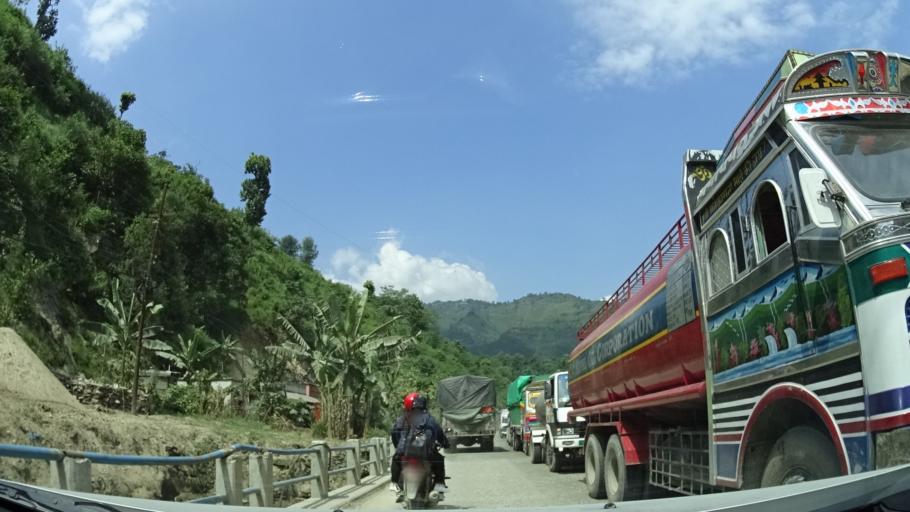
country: NP
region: Central Region
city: Kirtipur
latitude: 27.7973
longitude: 84.9944
